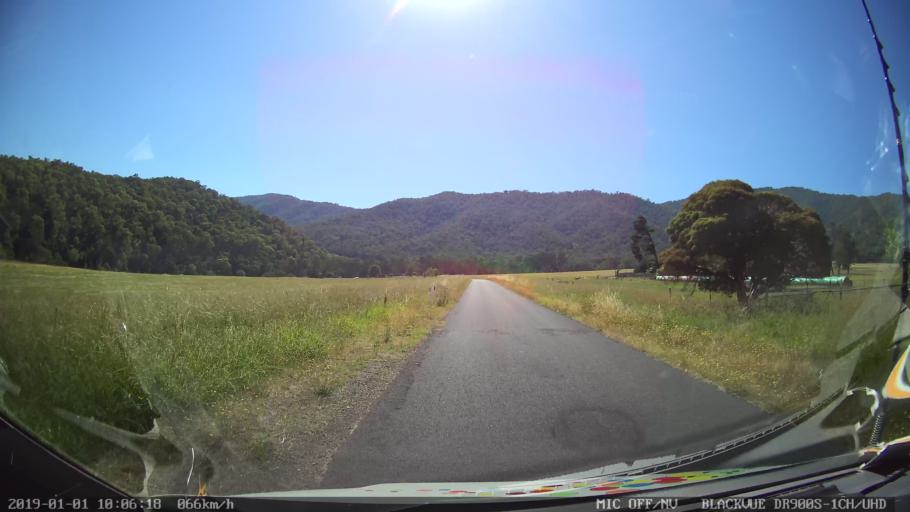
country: AU
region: New South Wales
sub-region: Snowy River
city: Jindabyne
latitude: -36.1743
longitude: 148.1459
